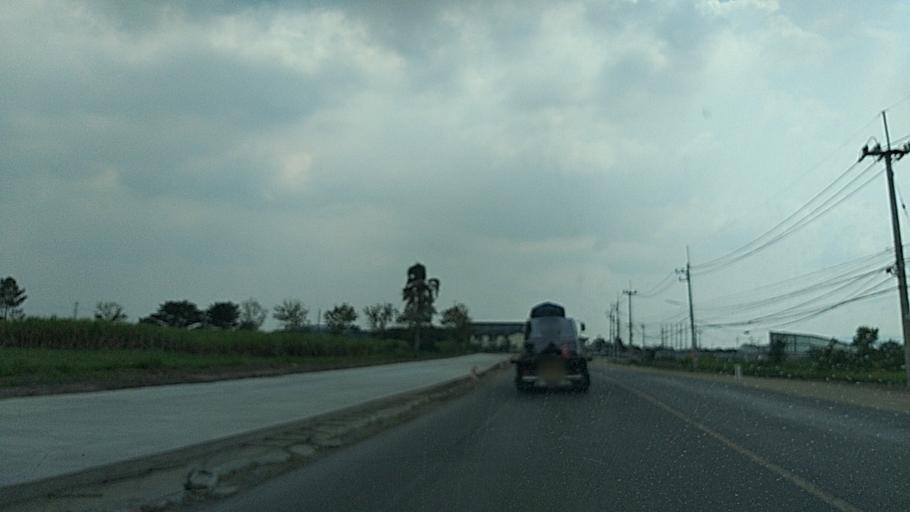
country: TH
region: Chon Buri
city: Ban Bueng
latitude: 13.2999
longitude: 101.1781
